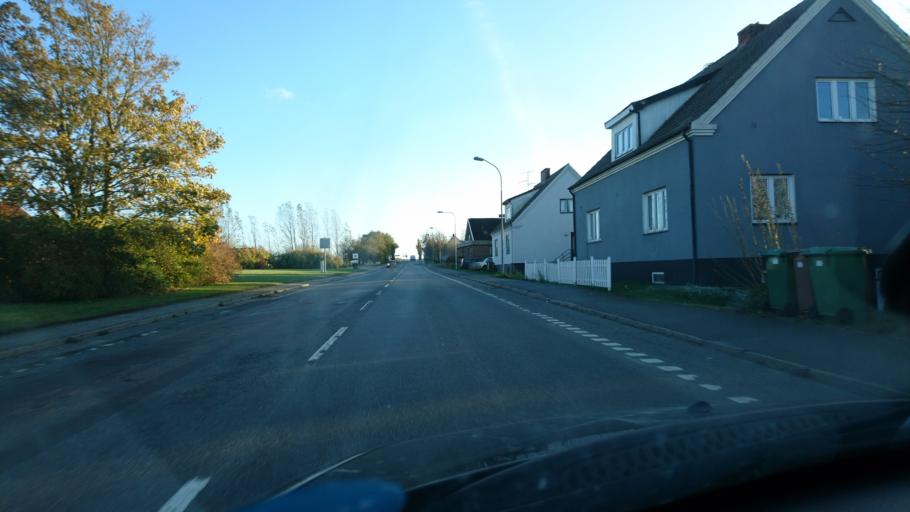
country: SE
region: Skane
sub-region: Tomelilla Kommun
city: Tomelilla
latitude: 55.5473
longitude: 14.1173
